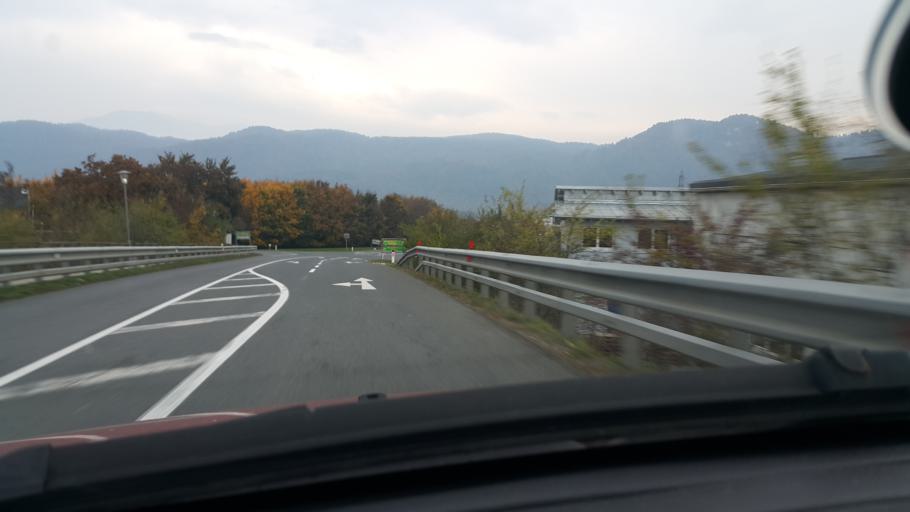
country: AT
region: Carinthia
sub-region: Politischer Bezirk Klagenfurt Land
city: Ebenthal
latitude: 46.6188
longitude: 14.3992
